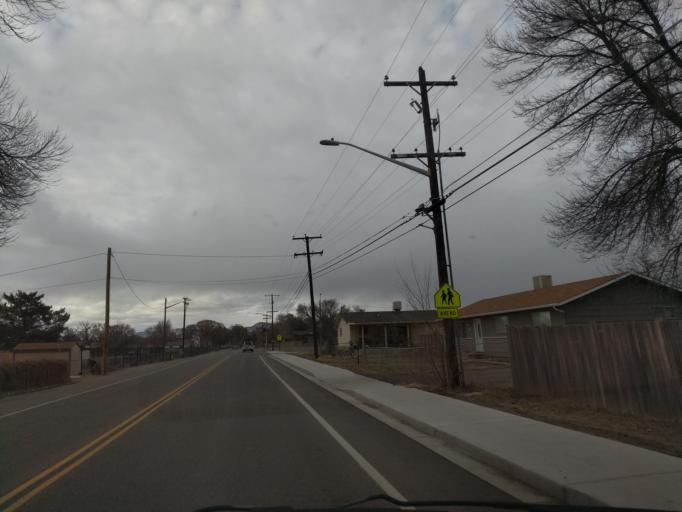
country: US
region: Colorado
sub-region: Mesa County
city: Fruitvale
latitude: 39.0820
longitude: -108.5198
